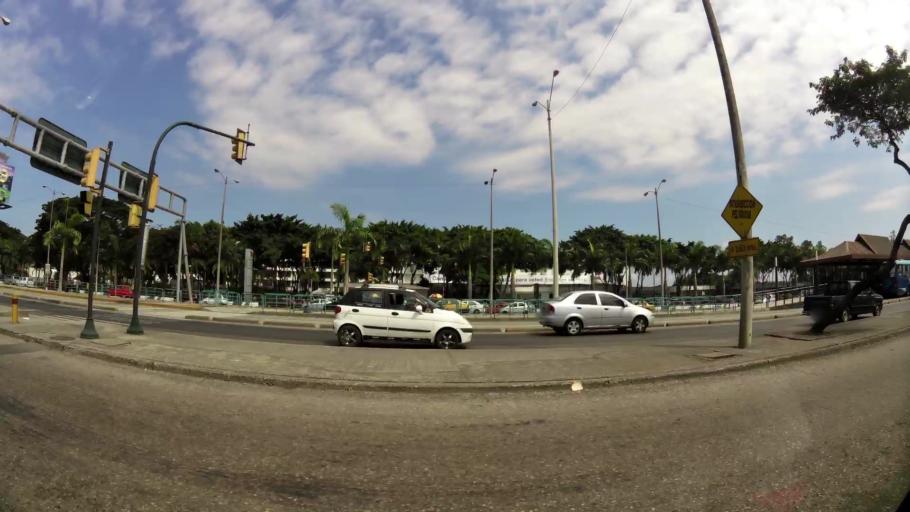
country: EC
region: Guayas
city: Guayaquil
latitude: -2.2326
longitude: -79.8970
